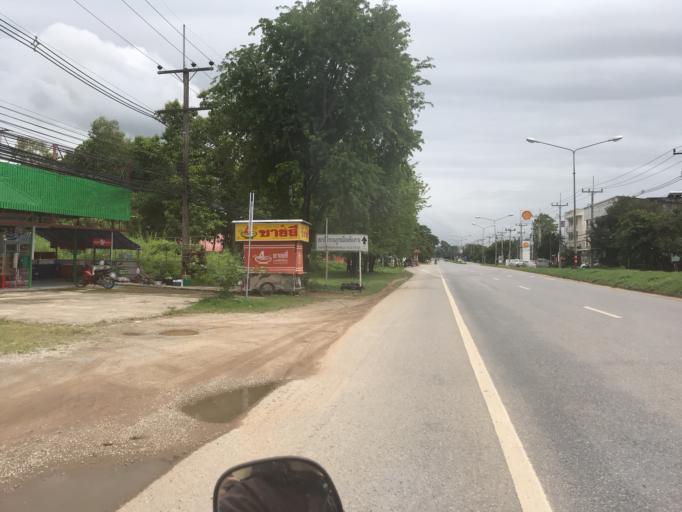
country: TH
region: Chiang Rai
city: Chiang Rai
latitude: 19.9466
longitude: 99.8476
